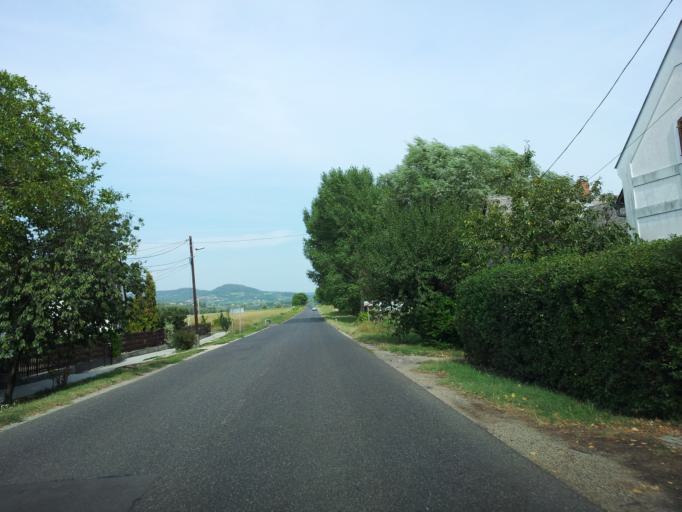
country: HU
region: Veszprem
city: Badacsonytomaj
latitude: 46.8389
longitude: 17.4876
